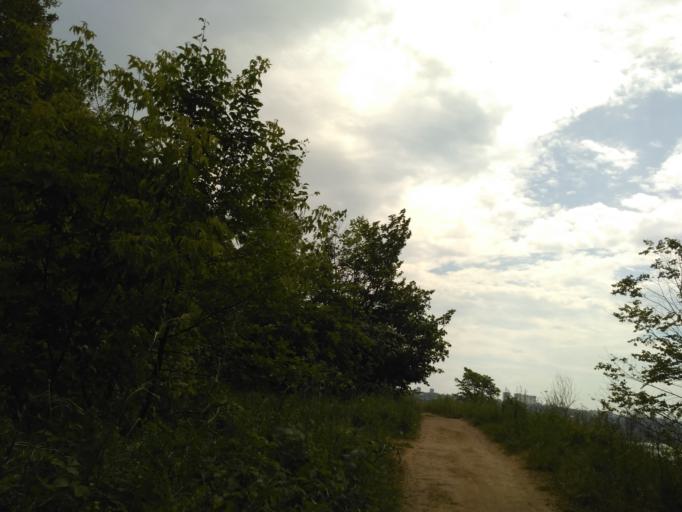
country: RU
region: Nizjnij Novgorod
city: Nizhniy Novgorod
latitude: 56.2762
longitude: 43.9712
